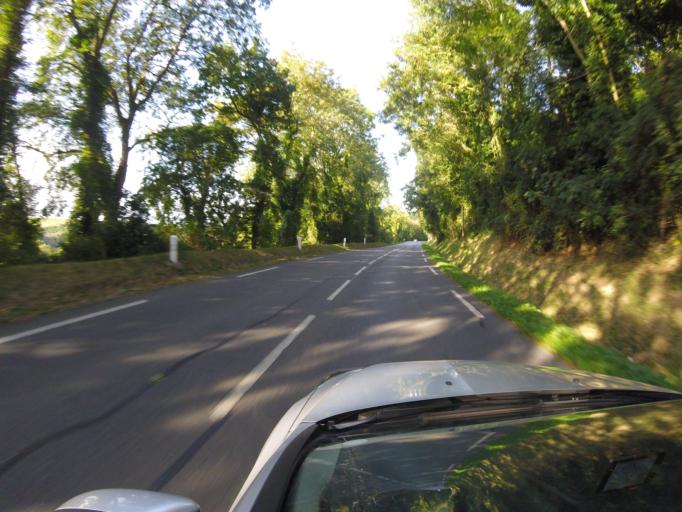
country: FR
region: Haute-Normandie
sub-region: Departement de la Seine-Maritime
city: Fecamp
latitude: 49.7625
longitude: 0.4007
